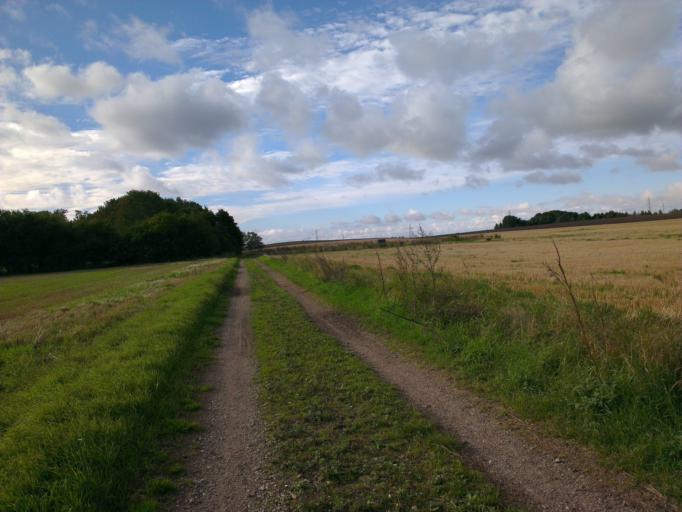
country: DK
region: Capital Region
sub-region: Frederikssund Kommune
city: Frederikssund
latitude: 55.8025
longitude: 12.0879
